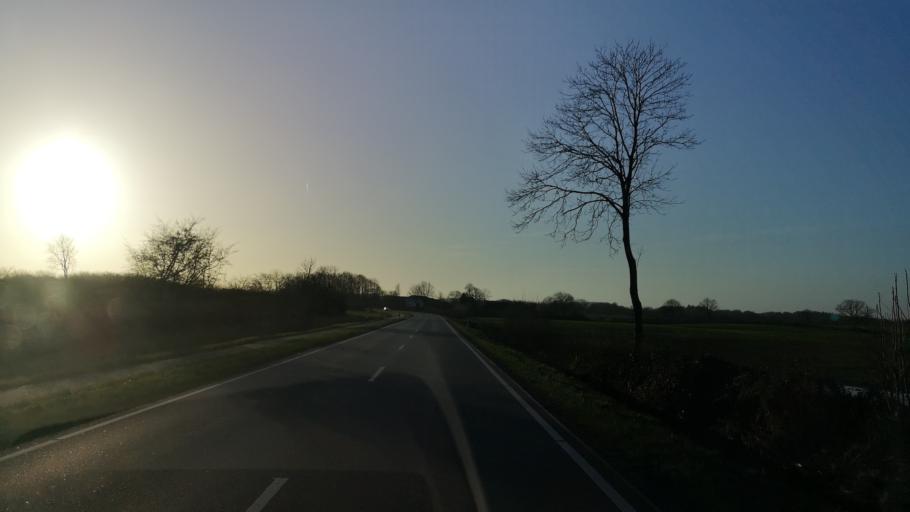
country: DE
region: Schleswig-Holstein
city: Grosssolt
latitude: 54.6942
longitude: 9.5025
